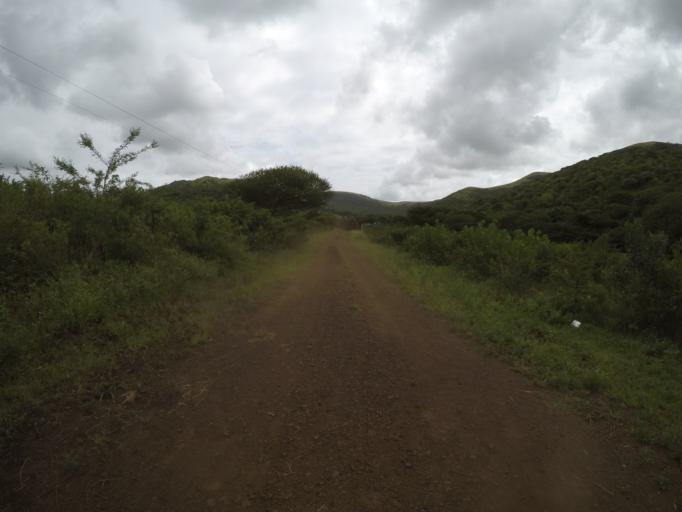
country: ZA
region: KwaZulu-Natal
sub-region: uThungulu District Municipality
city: Empangeni
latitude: -28.5845
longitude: 31.8893
